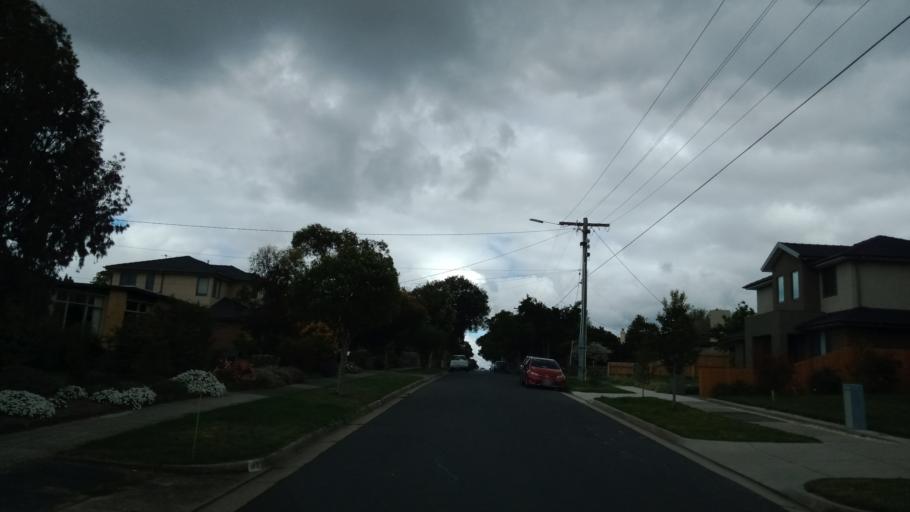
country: AU
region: Victoria
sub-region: Monash
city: Notting Hill
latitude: -37.8841
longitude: 145.1300
